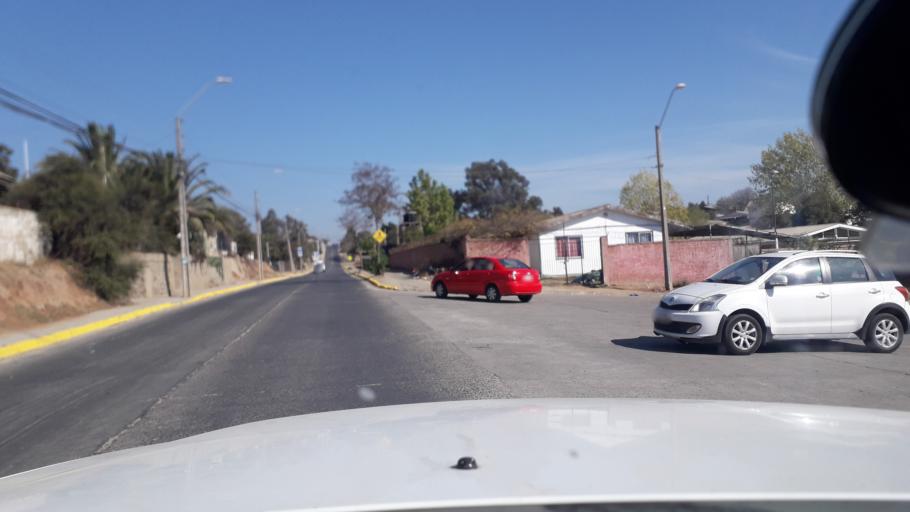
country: CL
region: Valparaiso
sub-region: Provincia de Marga Marga
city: Villa Alemana
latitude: -33.0606
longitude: -71.4024
